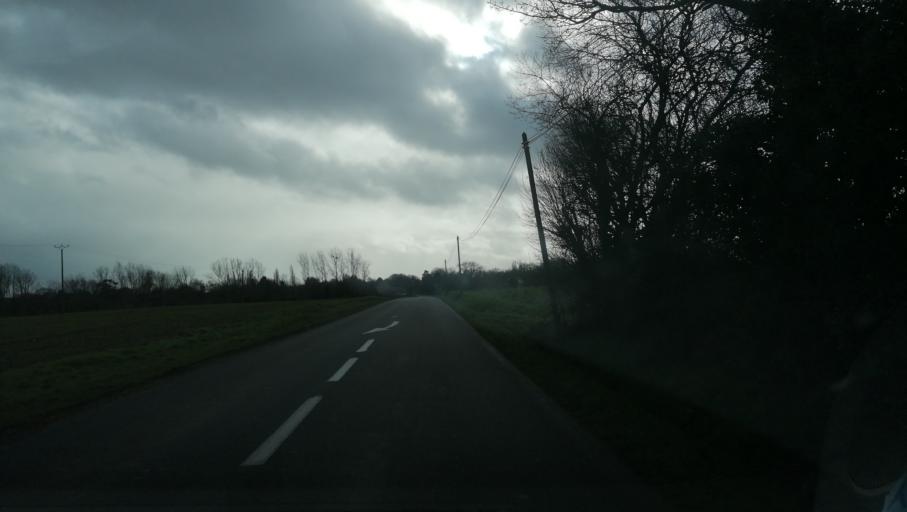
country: FR
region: Brittany
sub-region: Departement des Cotes-d'Armor
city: Lantic
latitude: 48.5864
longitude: -2.9157
